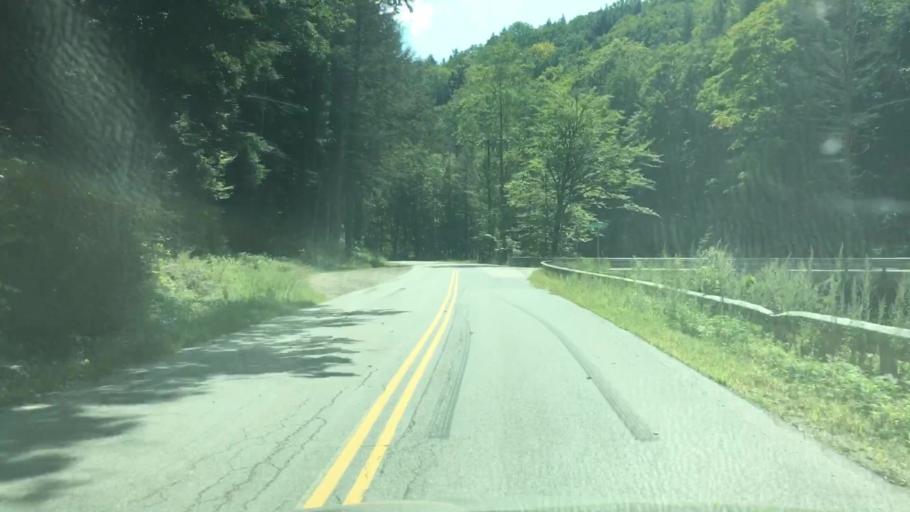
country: US
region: Vermont
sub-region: Windham County
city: West Brattleboro
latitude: 42.7985
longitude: -72.6836
